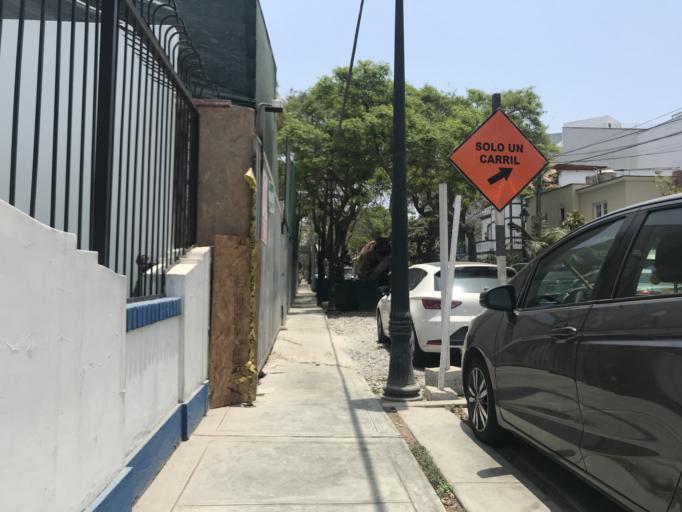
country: PE
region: Lima
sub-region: Lima
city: San Isidro
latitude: -12.1038
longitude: -77.0327
